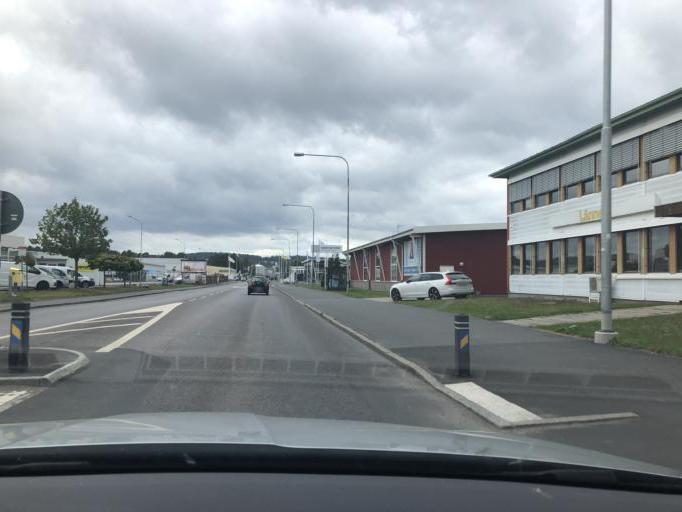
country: SE
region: Joenkoeping
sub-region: Jonkopings Kommun
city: Jonkoping
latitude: 57.7661
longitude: 14.1779
